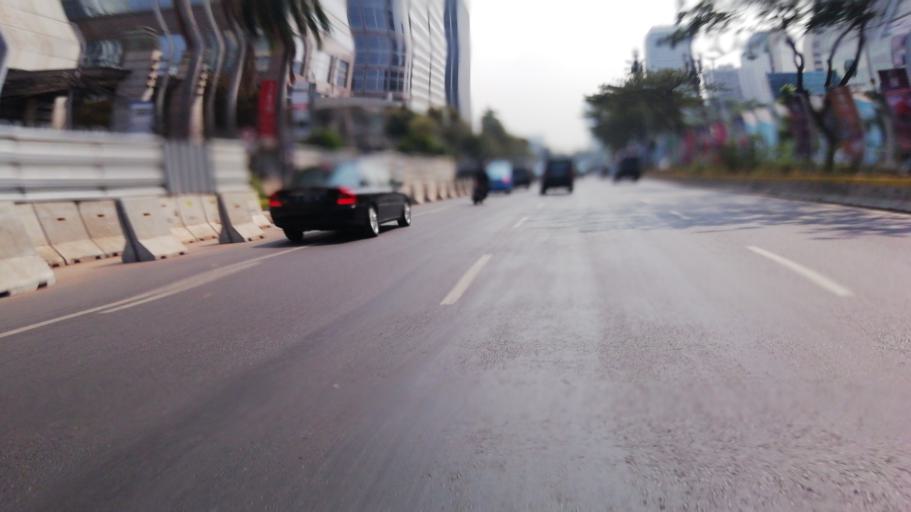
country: ID
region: Jakarta Raya
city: Jakarta
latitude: -6.2245
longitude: 106.8057
